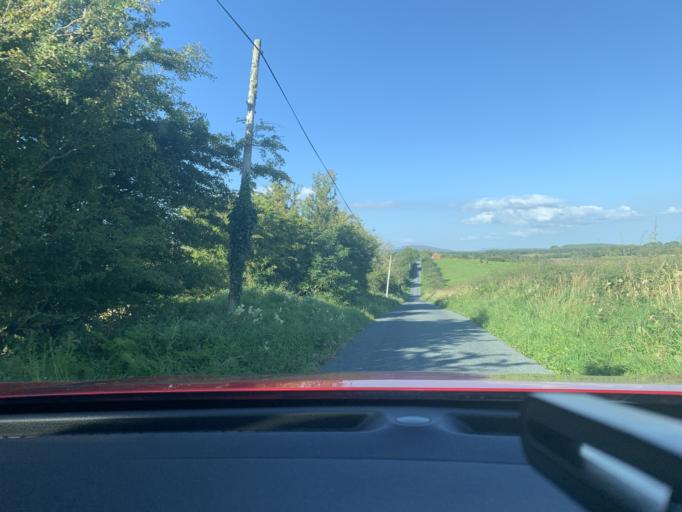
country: IE
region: Connaught
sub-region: Sligo
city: Tobercurry
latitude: 54.1457
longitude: -8.6798
